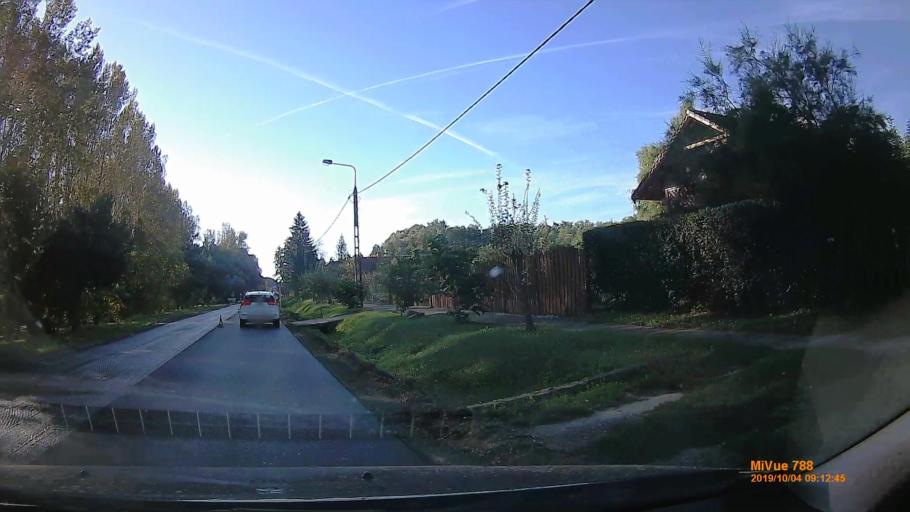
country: HU
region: Somogy
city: Karad
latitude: 46.6536
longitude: 17.7844
